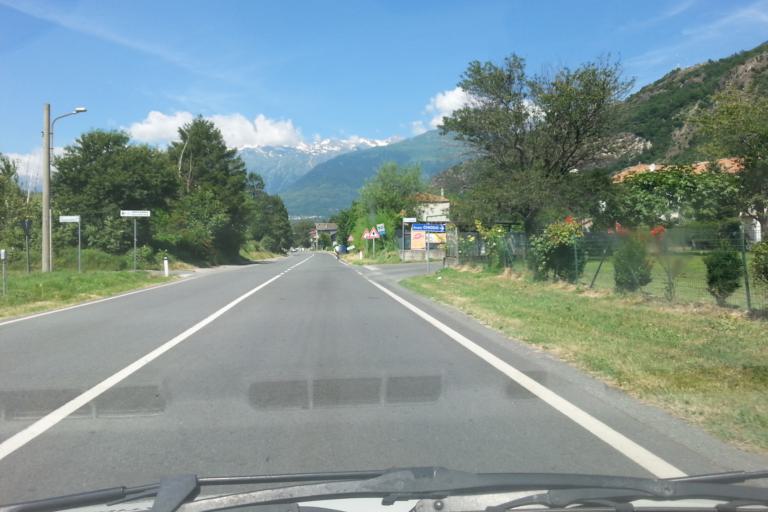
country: IT
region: Piedmont
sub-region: Provincia di Torino
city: Meana di Susa
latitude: 45.1386
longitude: 7.0864
